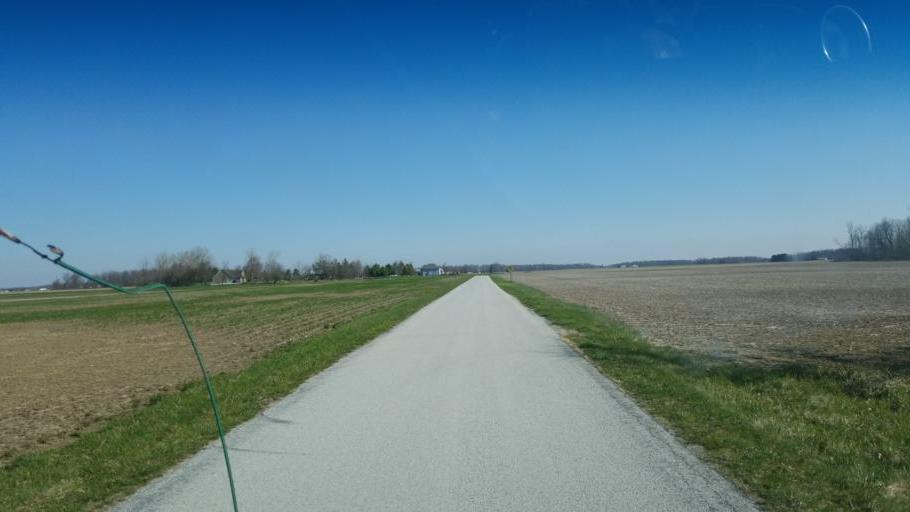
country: US
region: Ohio
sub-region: Hardin County
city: Kenton
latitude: 40.6913
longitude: -83.5592
